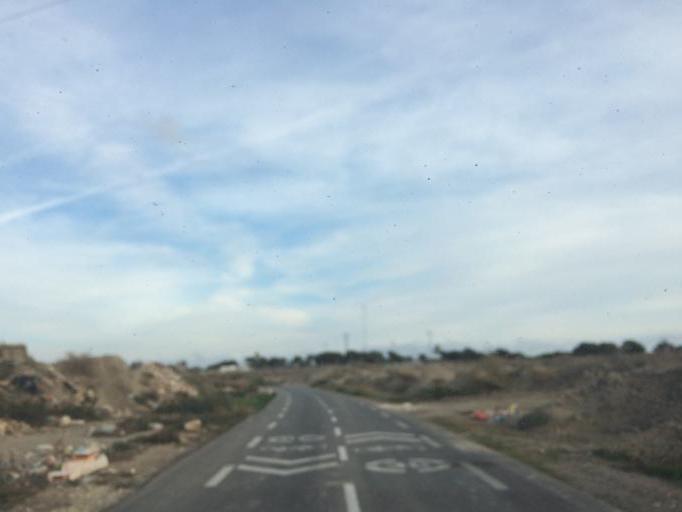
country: ES
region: Andalusia
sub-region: Provincia de Almeria
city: Almeria
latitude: 36.8316
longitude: -2.4357
